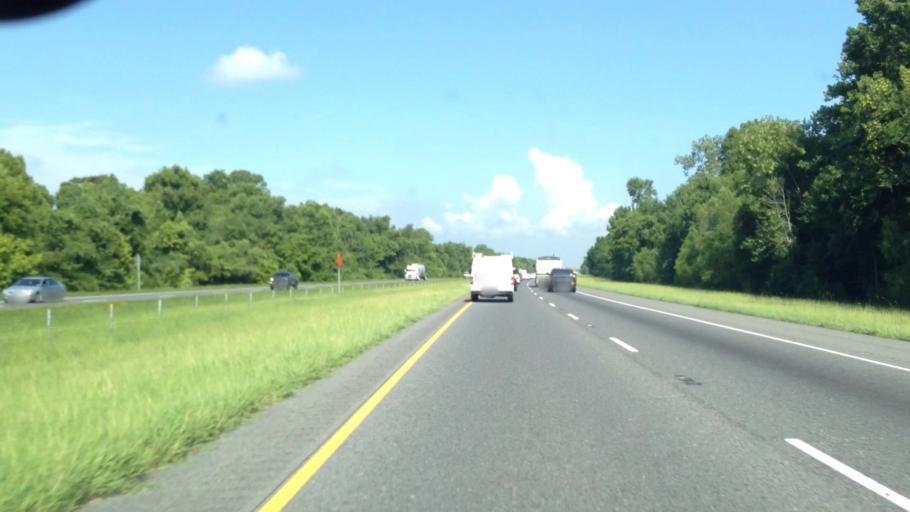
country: US
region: Louisiana
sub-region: Ascension Parish
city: Sorrento
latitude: 30.1554
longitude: -90.8169
